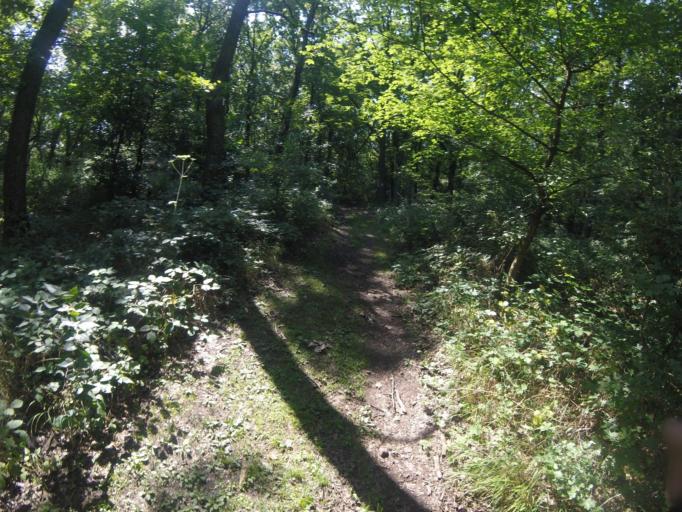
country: SK
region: Nitriansky
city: Sahy
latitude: 47.9880
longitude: 18.8889
